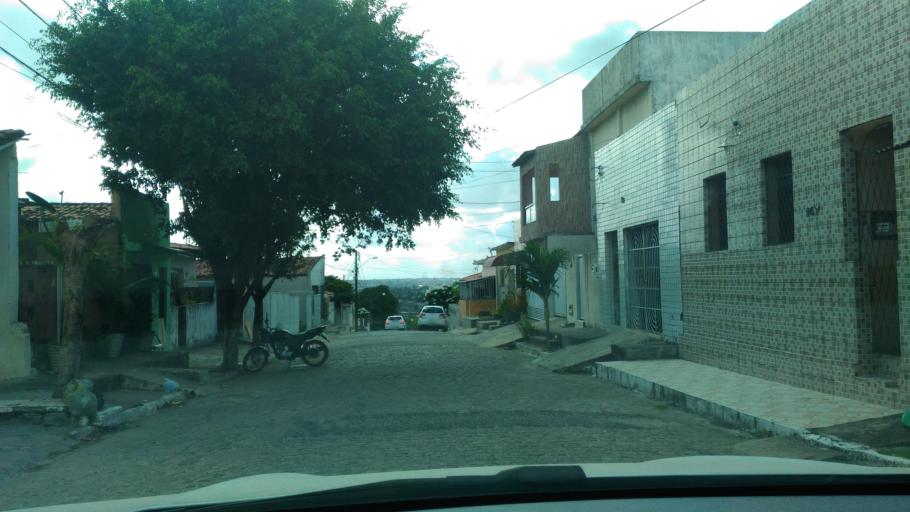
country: BR
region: Paraiba
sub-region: Joao Pessoa
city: Joao Pessoa
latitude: -7.1241
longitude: -34.8878
